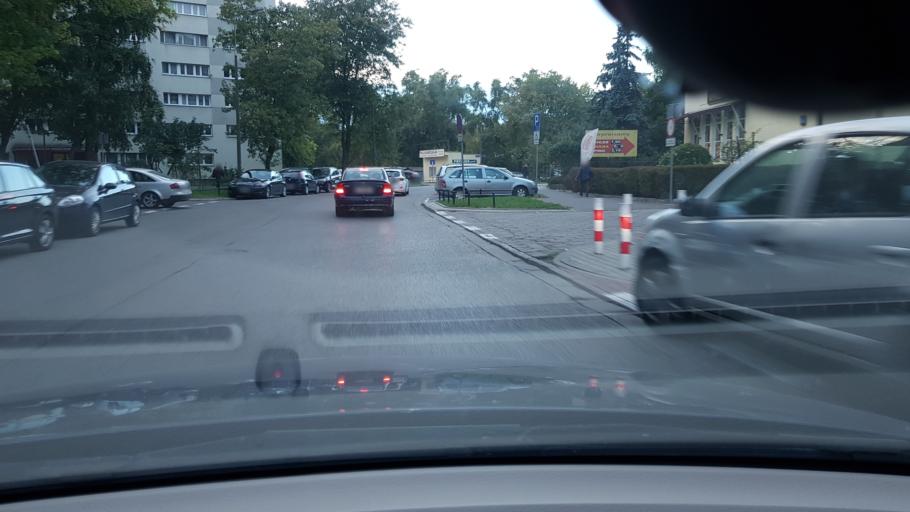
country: PL
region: Masovian Voivodeship
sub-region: Warszawa
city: Bielany
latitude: 52.2910
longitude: 20.9360
